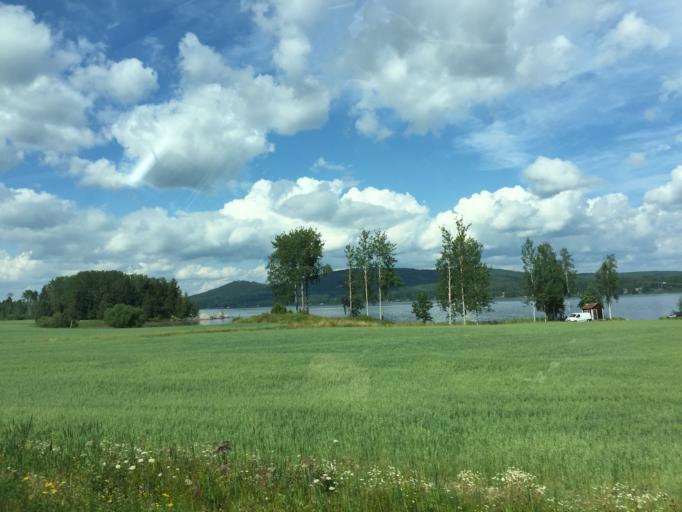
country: SE
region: Gaevleborg
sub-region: Bollnas Kommun
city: Kilafors
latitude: 61.1710
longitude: 16.8130
